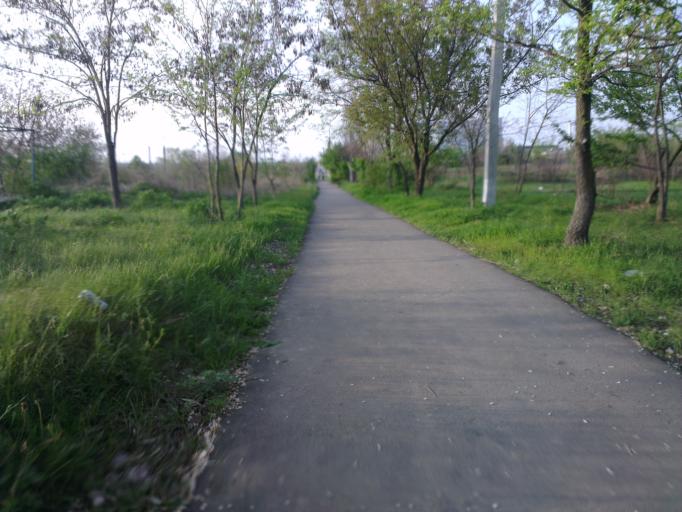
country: MD
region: Chisinau
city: Stauceni
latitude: 47.0668
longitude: 28.8871
